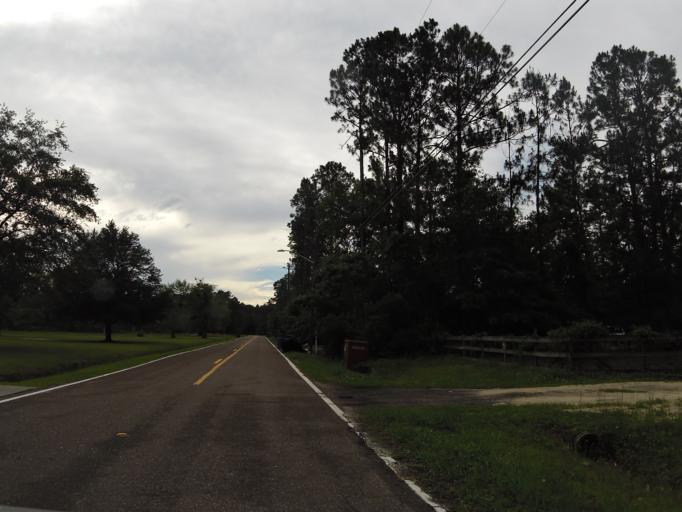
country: US
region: Florida
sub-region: Nassau County
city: Yulee
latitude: 30.5486
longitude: -81.6935
